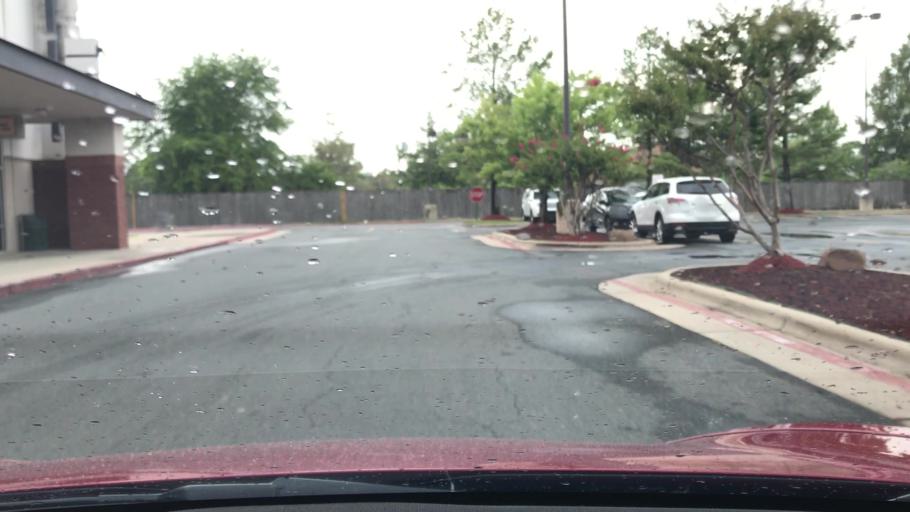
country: US
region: Louisiana
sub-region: Bossier Parish
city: Bossier City
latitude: 32.4426
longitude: -93.7212
